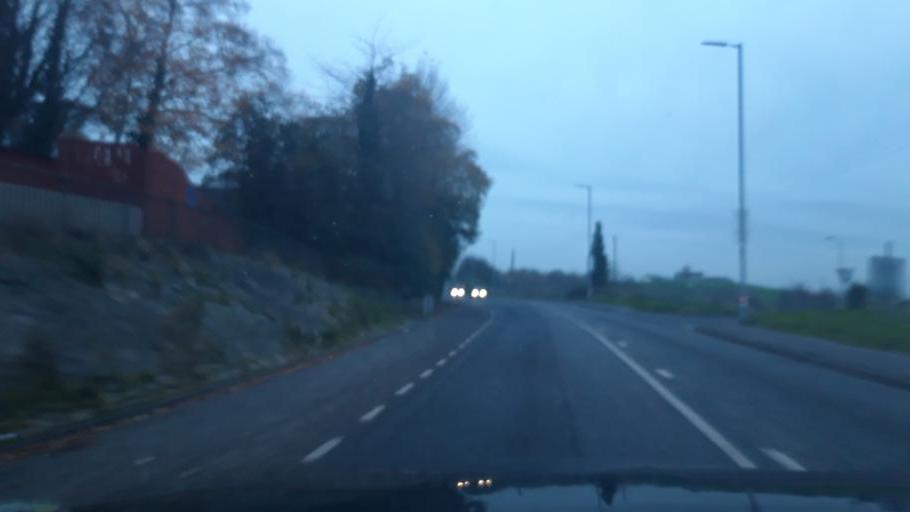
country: GB
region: Northern Ireland
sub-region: Newry and Mourne District
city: Newry
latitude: 54.1800
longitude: -6.3489
